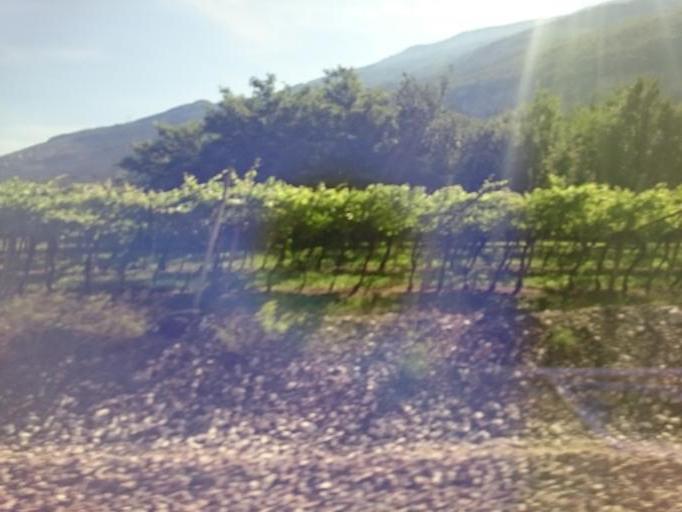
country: IT
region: Trentino-Alto Adige
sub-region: Provincia di Trento
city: Marco
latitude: 45.8268
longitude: 11.0043
